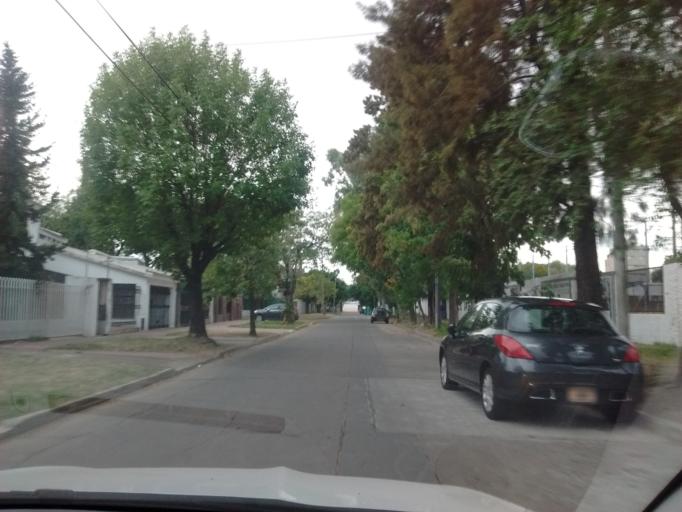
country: AR
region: Santa Fe
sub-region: Departamento de Rosario
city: Rosario
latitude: -32.9069
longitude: -60.6842
